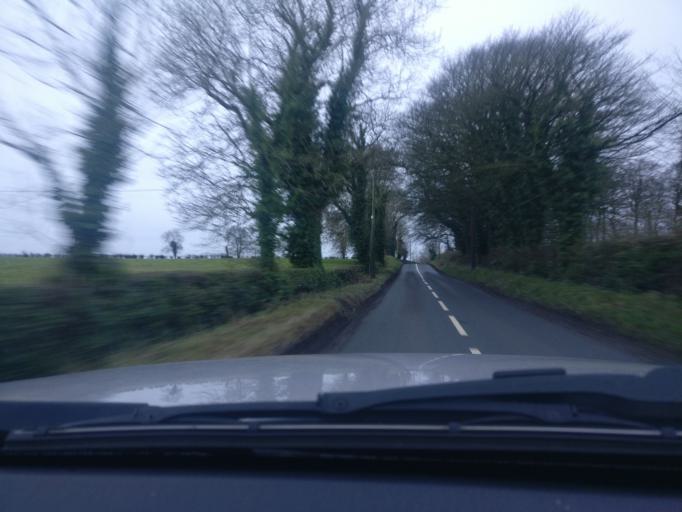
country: IE
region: Leinster
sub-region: An Mhi
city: Dunshaughlin
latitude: 53.4772
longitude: -6.6197
